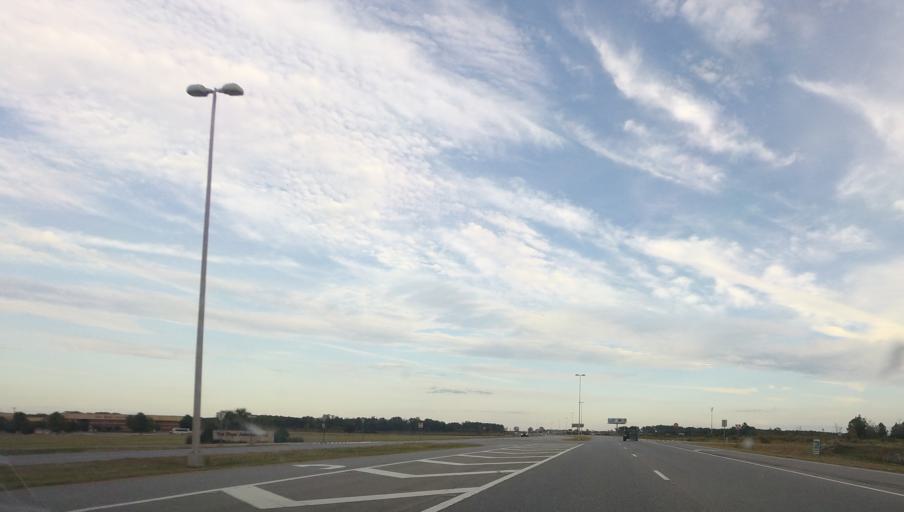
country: US
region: Georgia
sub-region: Houston County
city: Centerville
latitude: 32.5830
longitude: -83.7300
